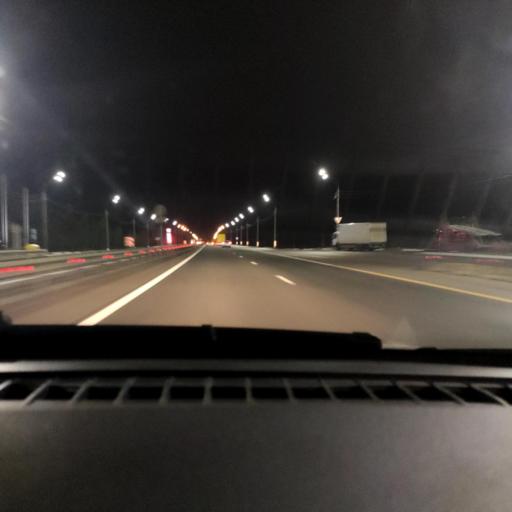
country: RU
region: Lipetsk
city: Khlevnoye
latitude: 52.2190
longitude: 39.1327
